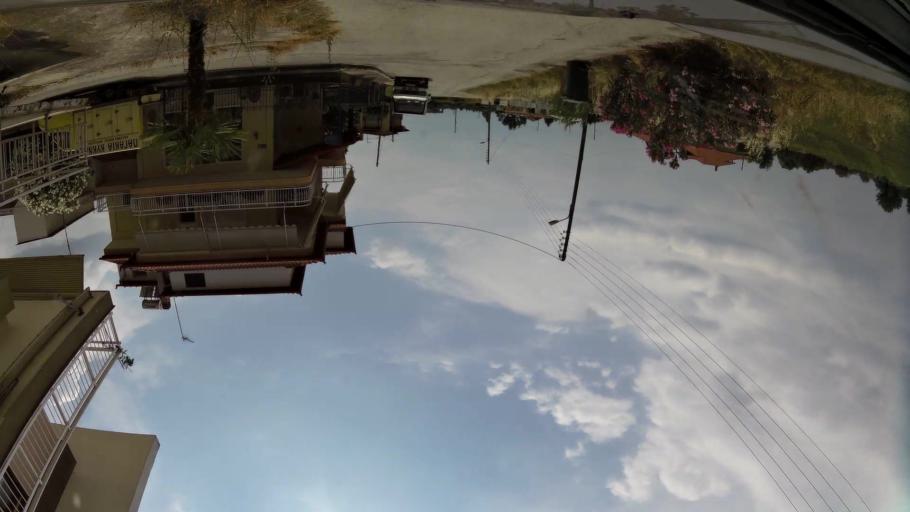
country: GR
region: Central Macedonia
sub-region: Nomos Pierias
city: Kallithea
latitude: 40.2685
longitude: 22.5813
